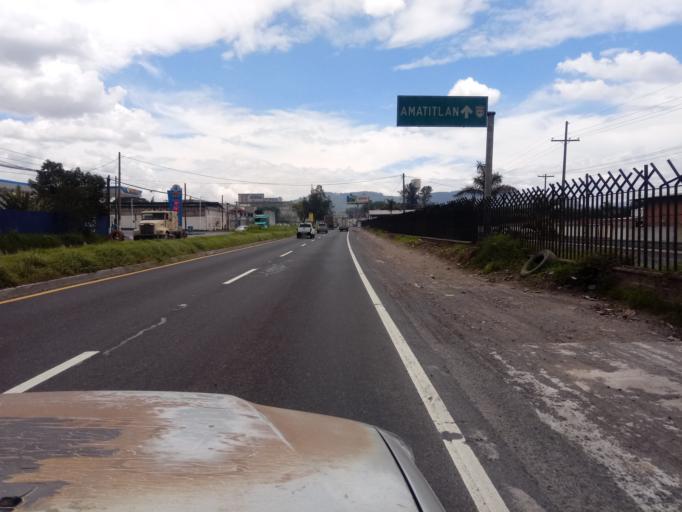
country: GT
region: Guatemala
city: Amatitlan
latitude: 14.4621
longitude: -90.6420
